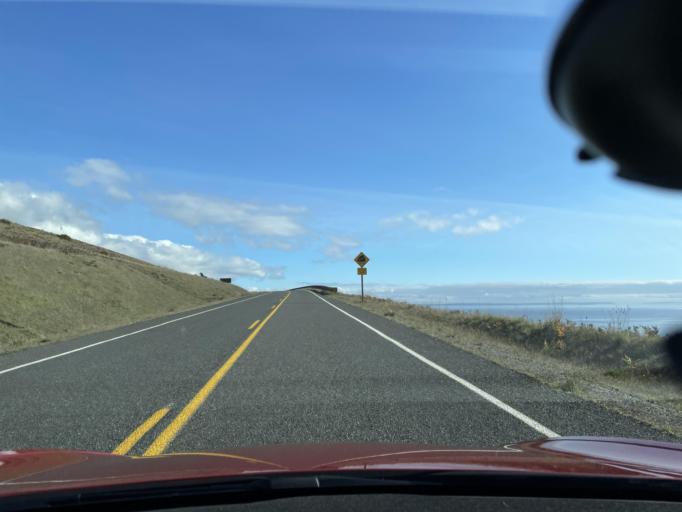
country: US
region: Washington
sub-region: San Juan County
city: Friday Harbor
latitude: 48.4557
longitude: -122.9776
